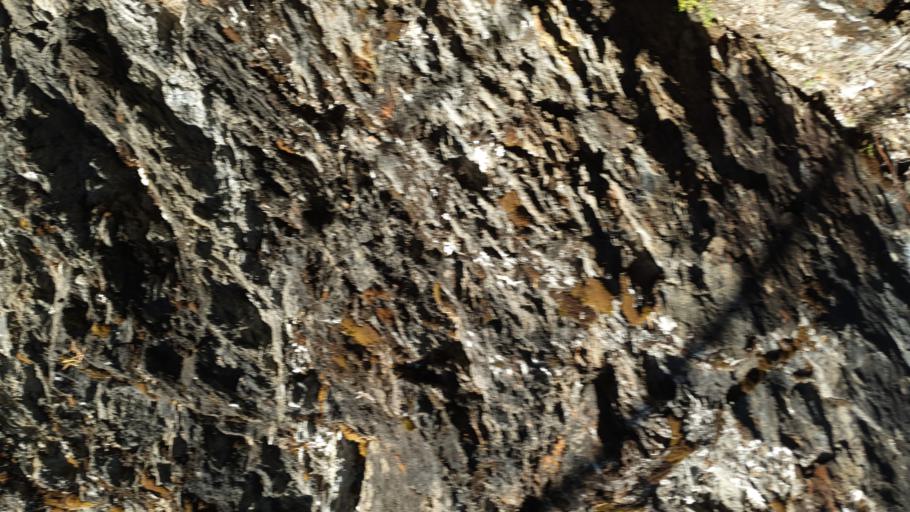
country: NO
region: Sor-Trondelag
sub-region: Meldal
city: Meldal
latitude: 63.1720
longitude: 9.7487
